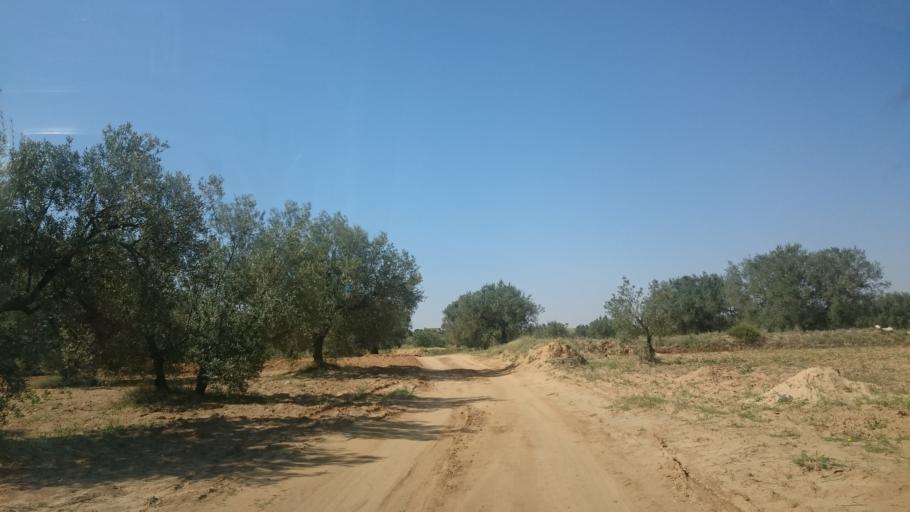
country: TN
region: Safaqis
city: Sfax
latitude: 34.7583
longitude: 10.5063
